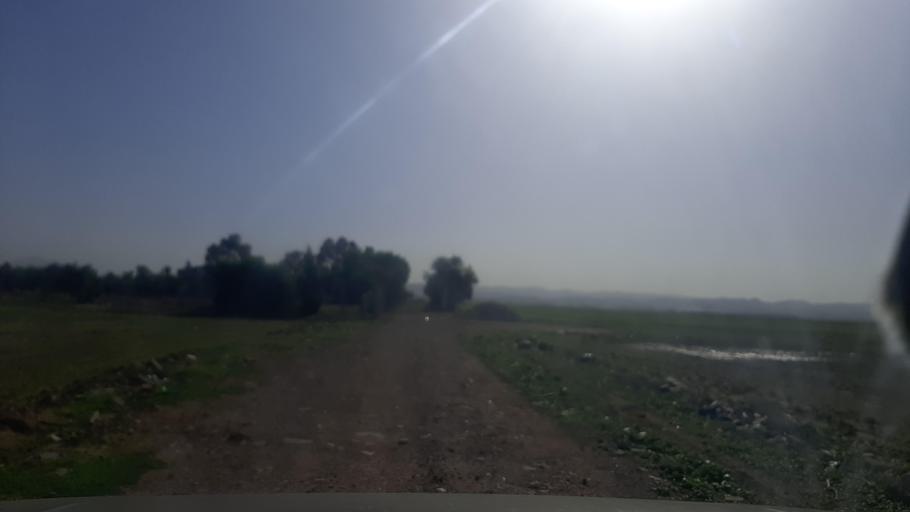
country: TN
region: Tunis
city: La Mohammedia
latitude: 36.6444
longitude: 10.0916
